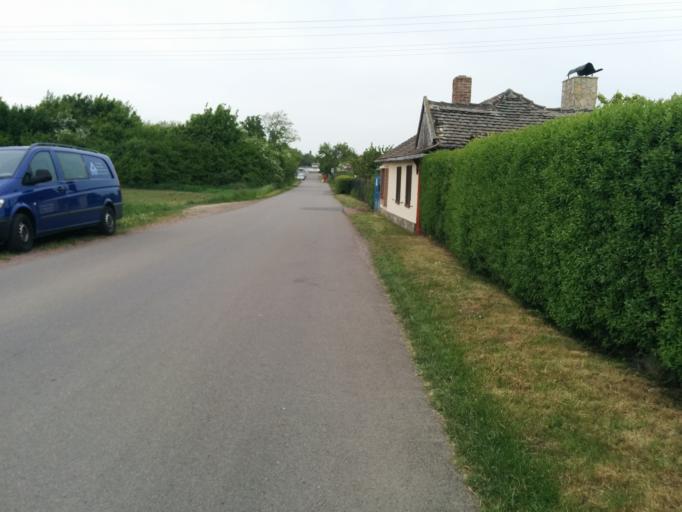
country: DE
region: Saxony-Anhalt
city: Zscherben
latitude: 51.4614
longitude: 11.8716
